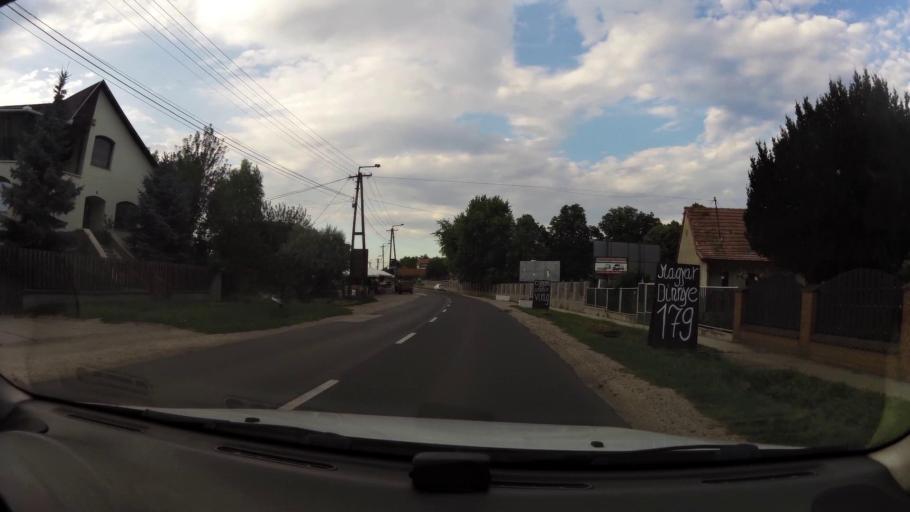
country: HU
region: Pest
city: Mende
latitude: 47.4307
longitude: 19.4601
